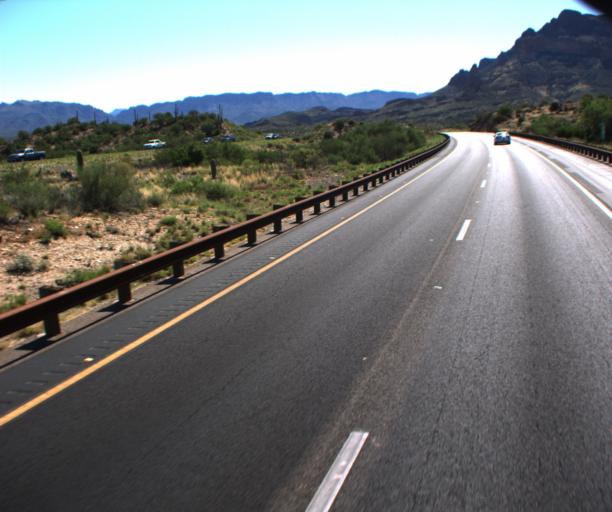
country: US
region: Arizona
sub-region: Pinal County
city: Superior
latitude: 33.2725
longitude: -111.1937
